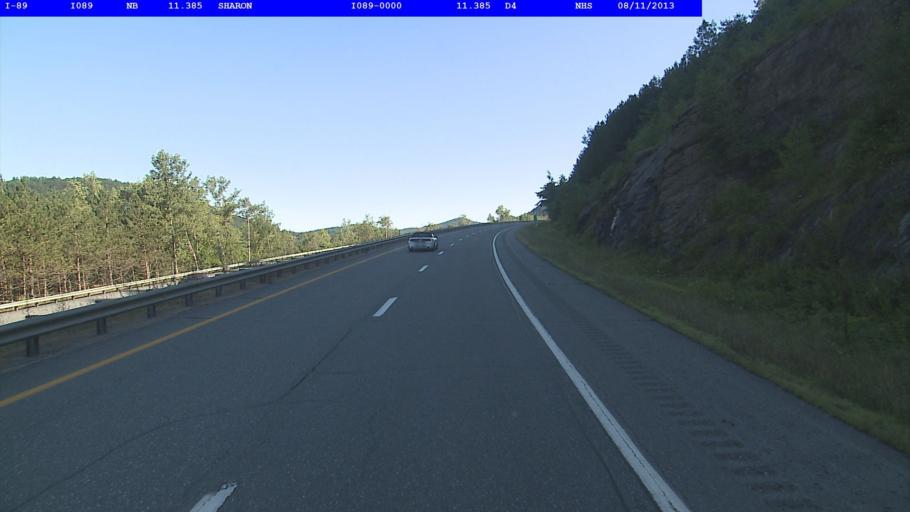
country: US
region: Vermont
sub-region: Windsor County
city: Woodstock
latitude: 43.7593
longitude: -72.4482
